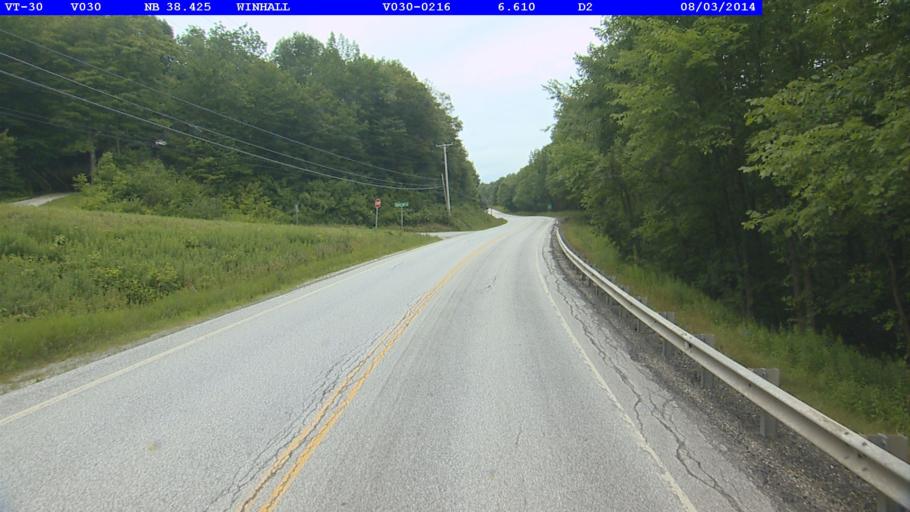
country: US
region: Vermont
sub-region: Bennington County
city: Manchester Center
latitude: 43.1937
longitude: -72.9533
